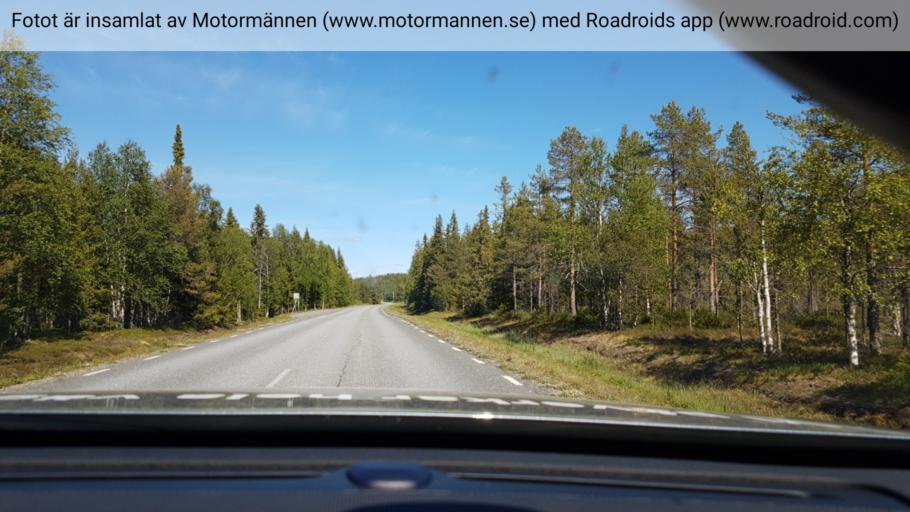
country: SE
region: Vaesterbotten
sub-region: Vilhelmina Kommun
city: Vilhelmina
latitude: 64.6552
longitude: 17.0888
